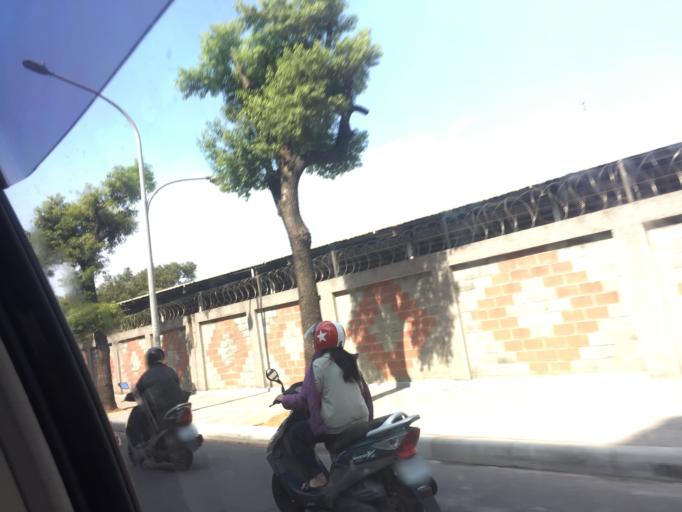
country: TW
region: Taiwan
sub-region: Taoyuan
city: Taoyuan
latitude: 24.9577
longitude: 121.3043
